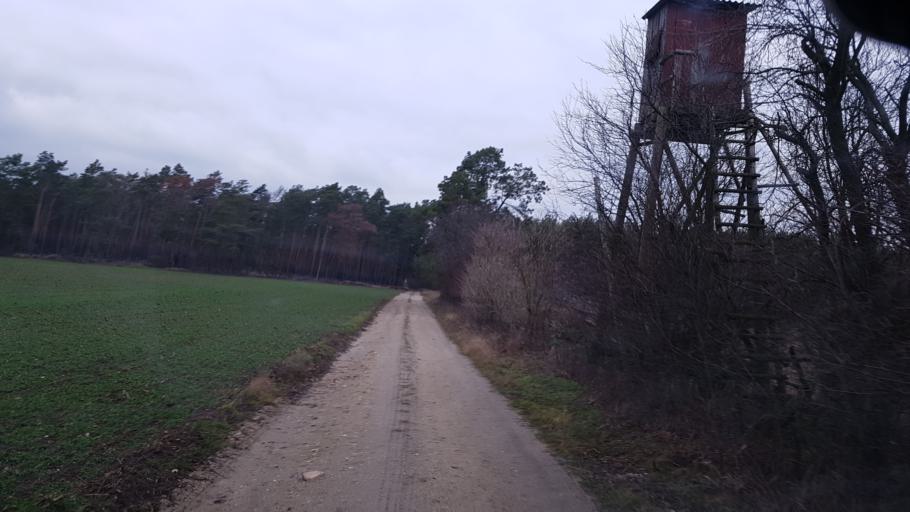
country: DE
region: Brandenburg
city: Finsterwalde
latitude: 51.6160
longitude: 13.6491
